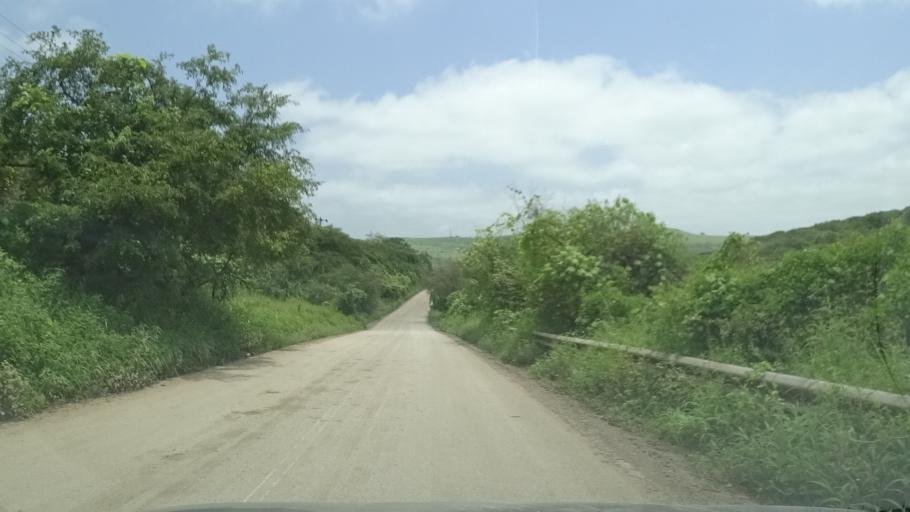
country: OM
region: Zufar
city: Salalah
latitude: 17.1959
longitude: 54.1766
